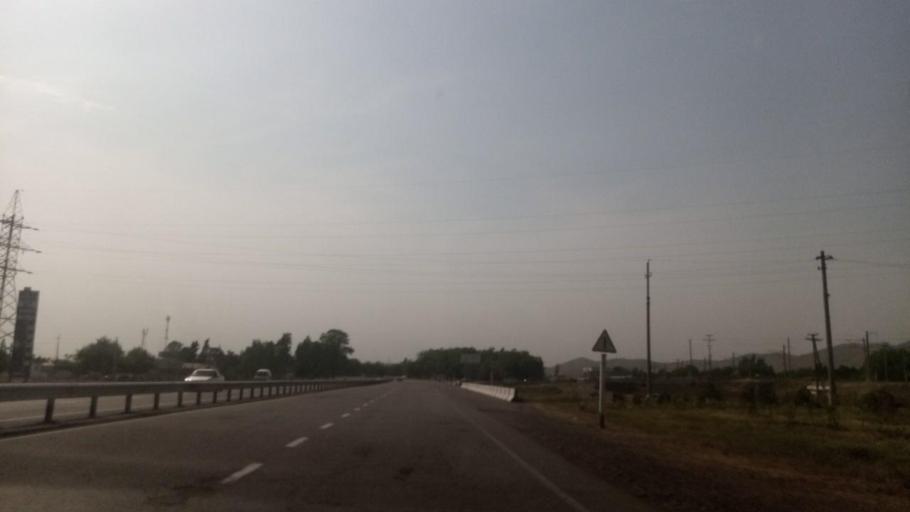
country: UZ
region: Toshkent
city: Ohangaron
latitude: 40.9084
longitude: 69.7935
